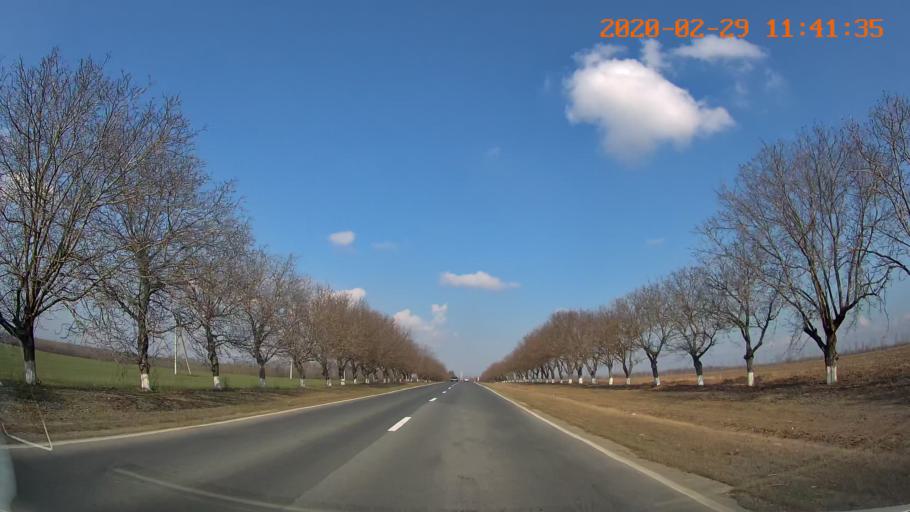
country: MD
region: Rezina
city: Saharna
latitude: 47.6734
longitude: 29.0160
